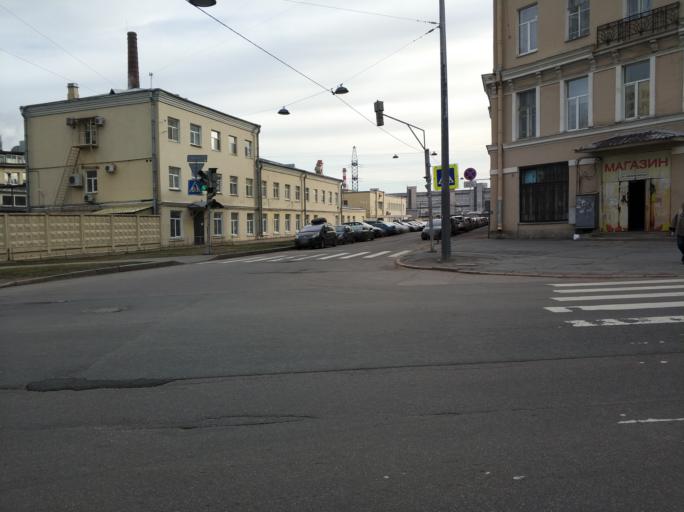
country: RU
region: St.-Petersburg
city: Saint Petersburg
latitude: 59.9046
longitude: 30.3267
